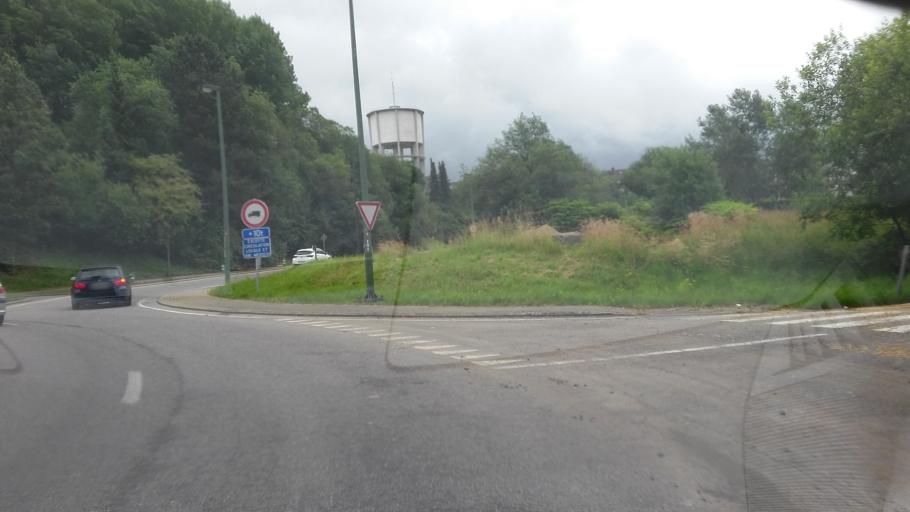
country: BE
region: Wallonia
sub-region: Province du Luxembourg
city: Arlon
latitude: 49.6884
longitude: 5.8189
